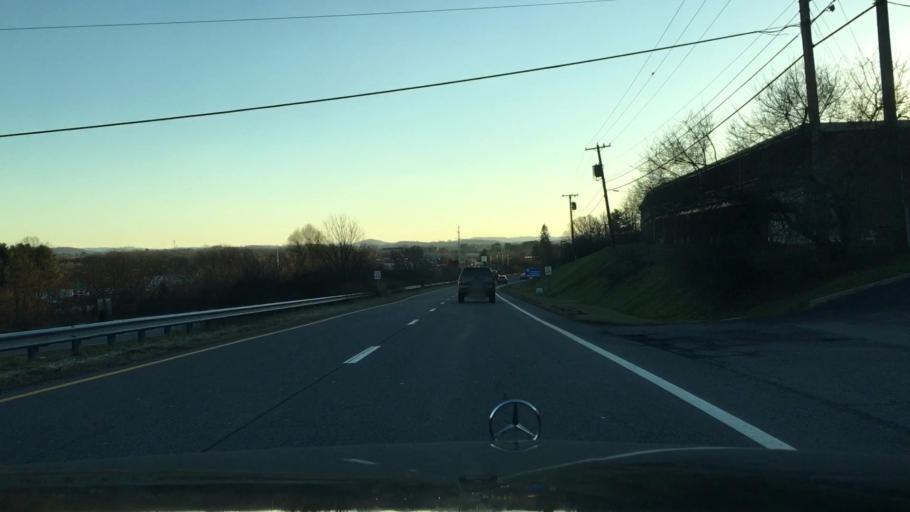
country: US
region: Virginia
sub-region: Montgomery County
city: Merrimac
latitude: 37.1832
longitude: -80.4103
